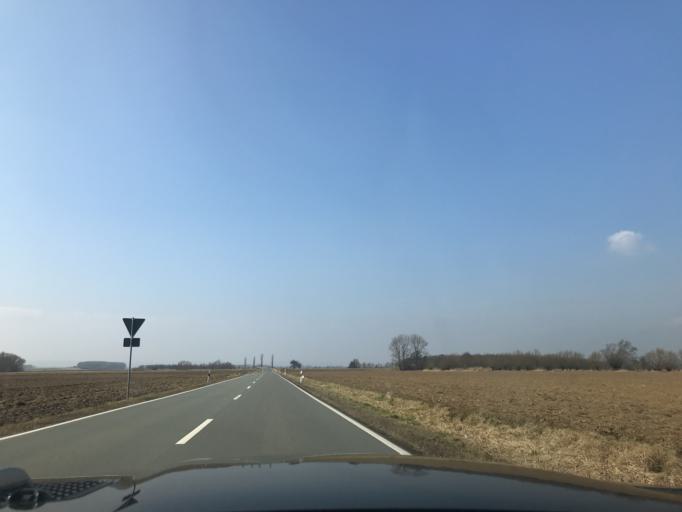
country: DE
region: Thuringia
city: Bad Langensalza
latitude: 51.1375
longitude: 10.6296
